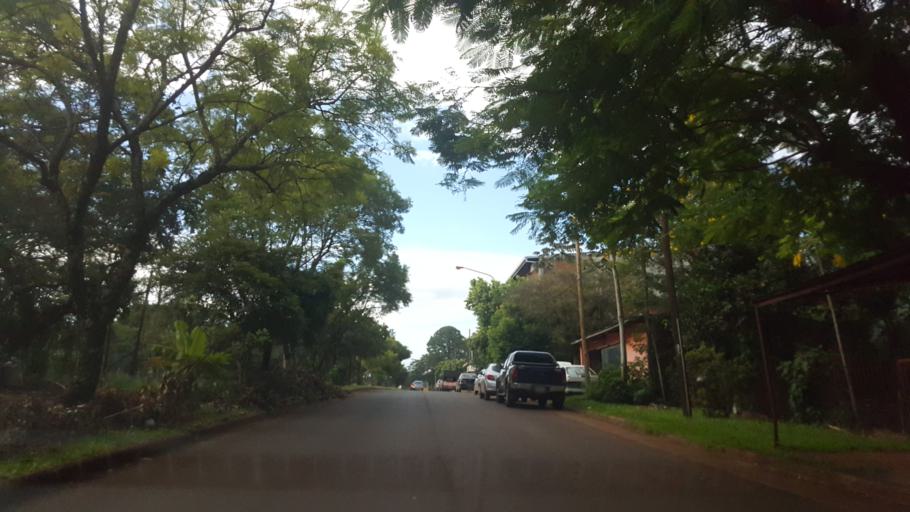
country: AR
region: Misiones
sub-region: Departamento de Capital
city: Posadas
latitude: -27.3689
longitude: -55.9319
